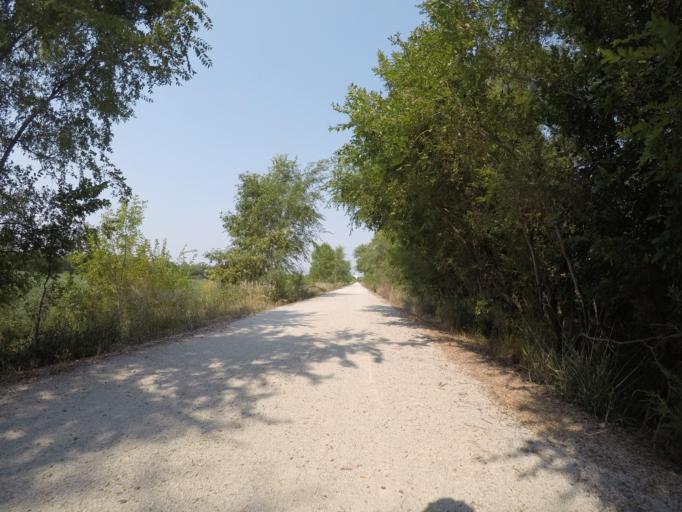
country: US
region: Nebraska
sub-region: Gage County
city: Beatrice
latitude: 40.2552
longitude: -96.7353
